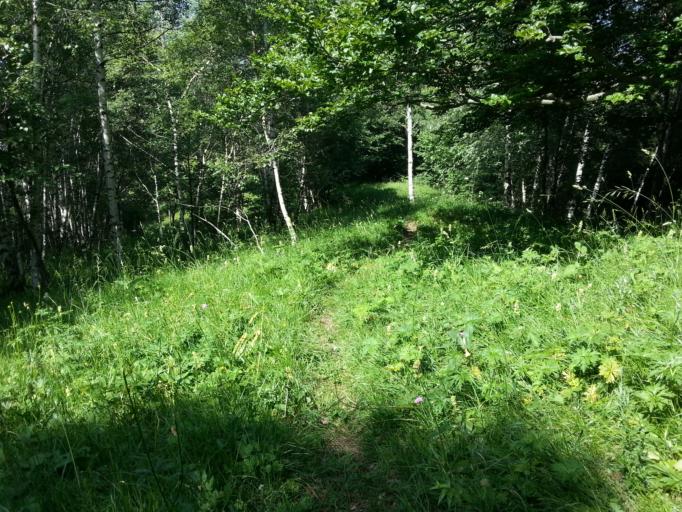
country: IT
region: Lombardy
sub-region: Provincia di Lecco
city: Ballabio
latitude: 45.9115
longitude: 9.4491
